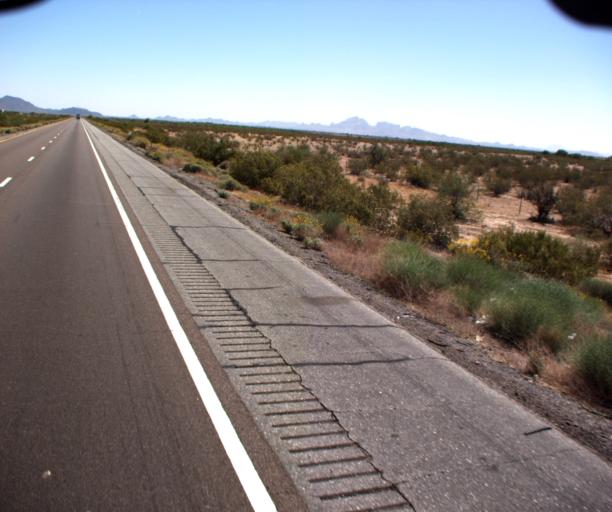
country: US
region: Arizona
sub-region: La Paz County
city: Salome
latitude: 33.5491
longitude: -113.2241
